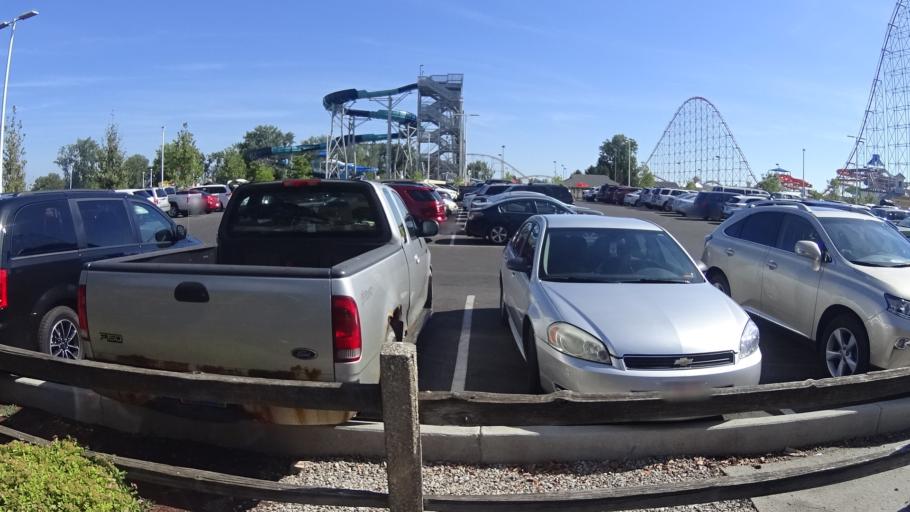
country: US
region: Ohio
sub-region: Erie County
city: Sandusky
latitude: 41.4865
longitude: -82.6876
